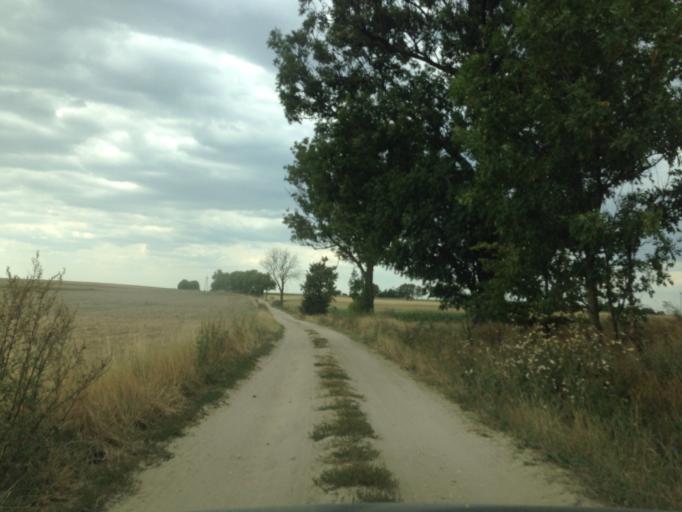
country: PL
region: Kujawsko-Pomorskie
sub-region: Powiat chelminski
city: Lisewo
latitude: 53.2893
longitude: 18.5916
